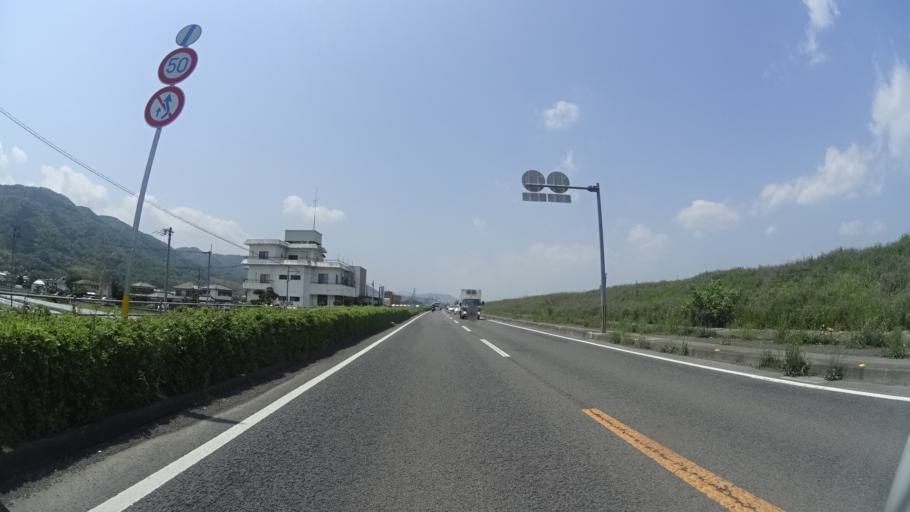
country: JP
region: Tokushima
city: Kamojimacho-jogejima
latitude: 34.0607
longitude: 134.3093
